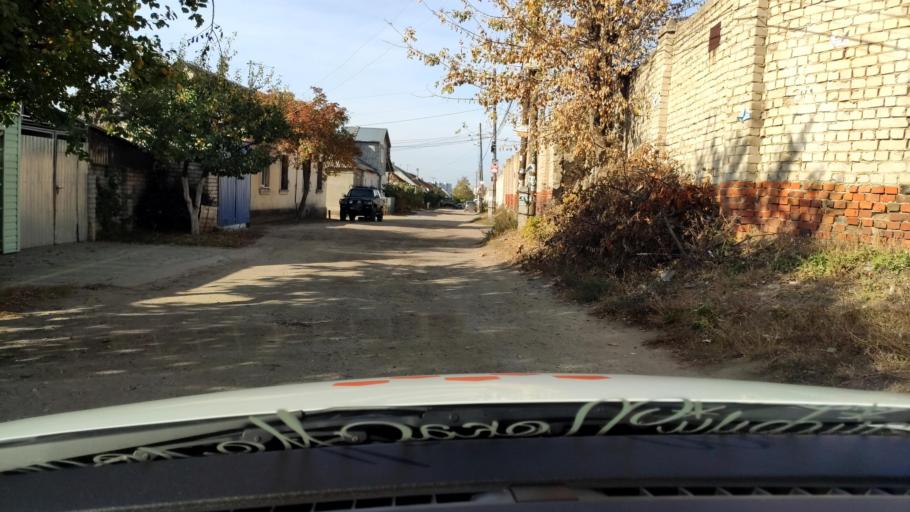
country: RU
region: Voronezj
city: Voronezh
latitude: 51.6692
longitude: 39.1572
